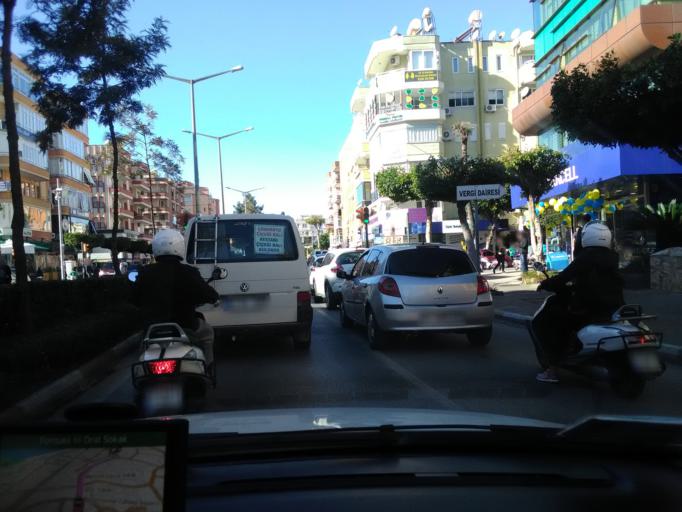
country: TR
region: Antalya
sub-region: Alanya
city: Alanya
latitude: 36.5474
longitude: 31.9968
